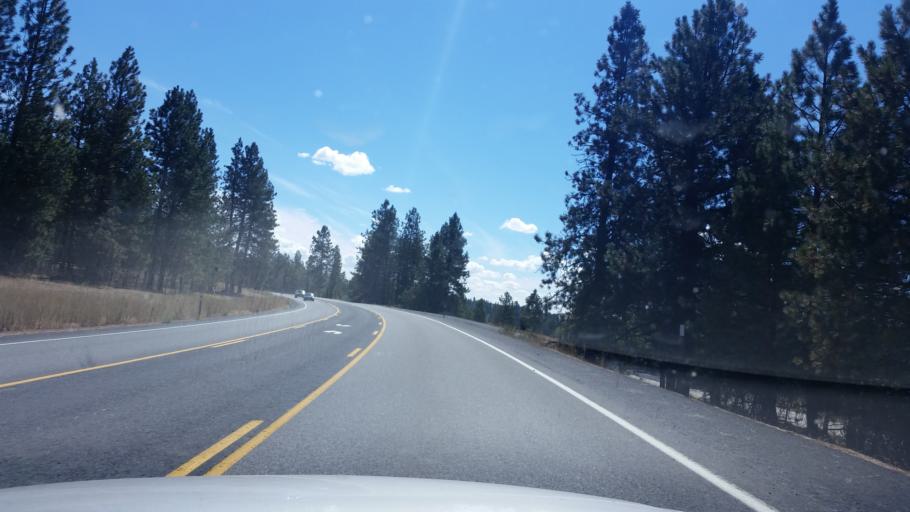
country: US
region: Washington
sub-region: Spokane County
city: Cheney
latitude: 47.5559
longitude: -117.5943
